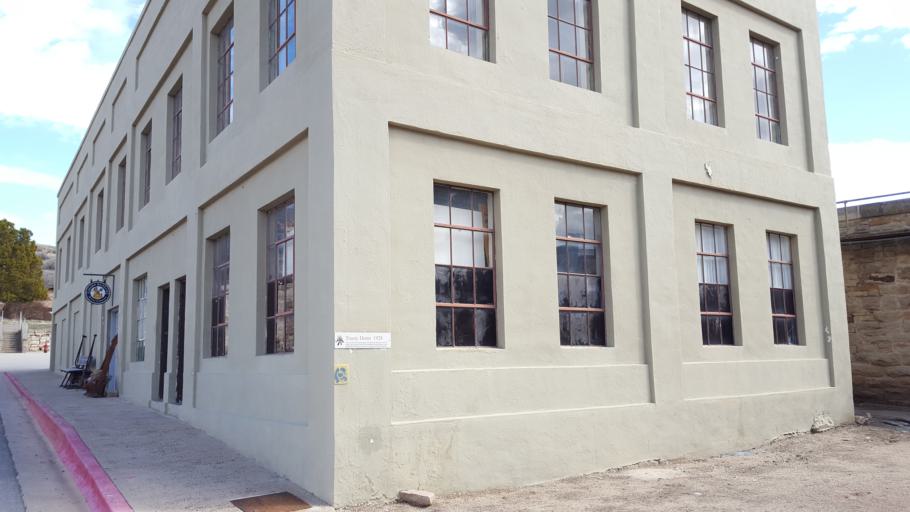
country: US
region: Idaho
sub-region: Ada County
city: Boise
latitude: 43.6031
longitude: -116.1617
